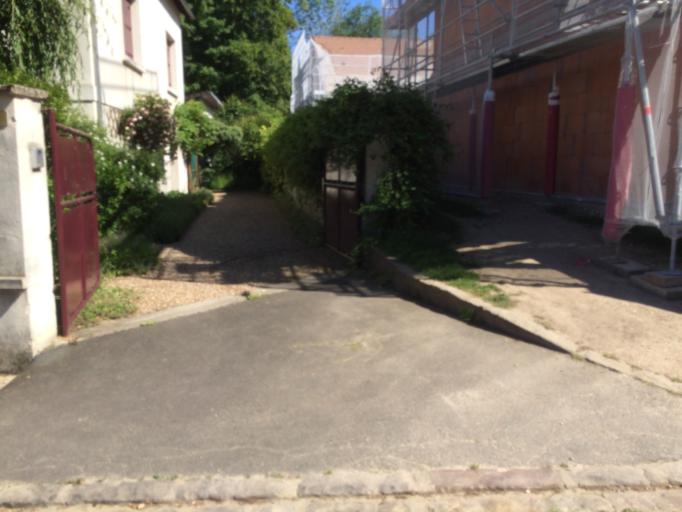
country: FR
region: Ile-de-France
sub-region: Departement de l'Essonne
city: Vauhallan
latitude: 48.7318
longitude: 2.2051
